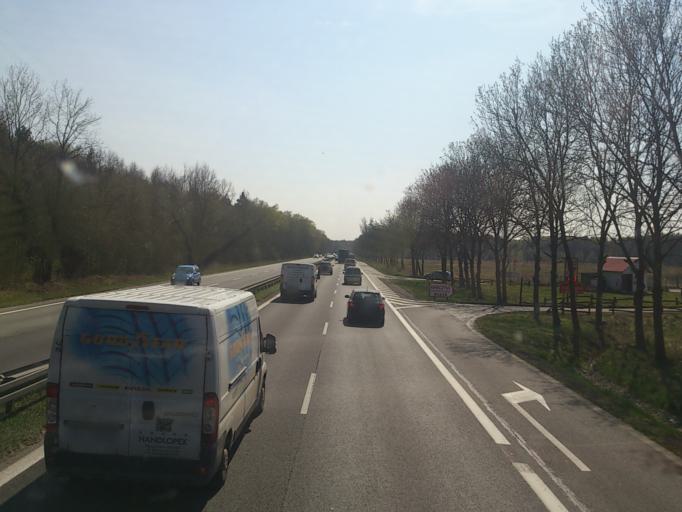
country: PL
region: Silesian Voivodeship
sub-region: Powiat bedzinski
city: Sarnow
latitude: 50.3966
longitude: 19.1889
